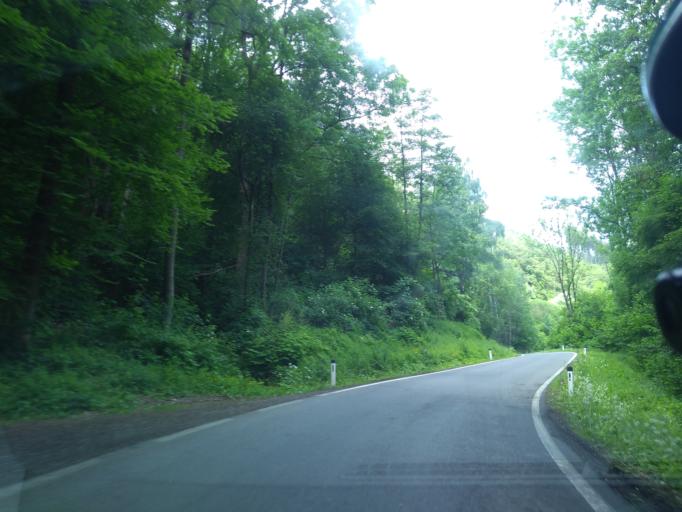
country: AT
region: Styria
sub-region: Politischer Bezirk Bruck-Muerzzuschlag
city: Bruck an der Mur
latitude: 47.3919
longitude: 15.2861
